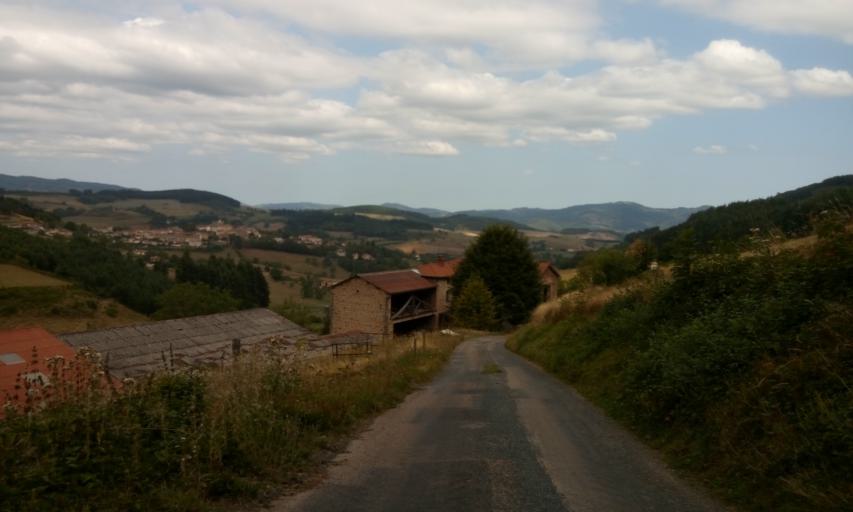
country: FR
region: Rhone-Alpes
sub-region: Departement du Rhone
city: Grandris
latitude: 45.9886
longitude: 4.4429
